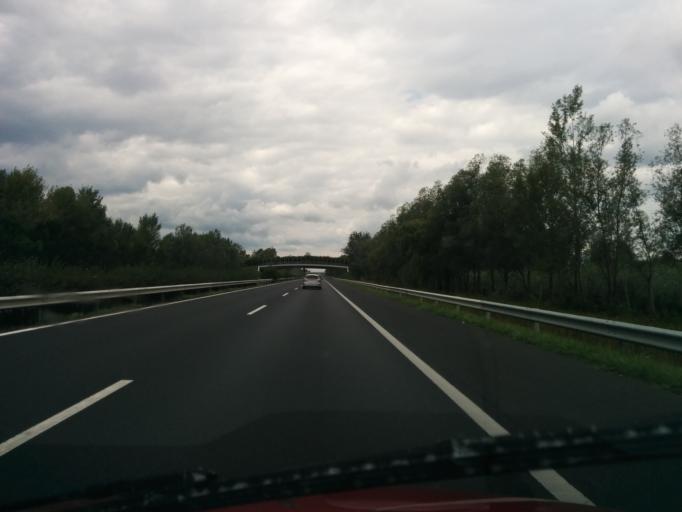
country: HU
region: Gyor-Moson-Sopron
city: Kimle
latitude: 47.7770
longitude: 17.3588
